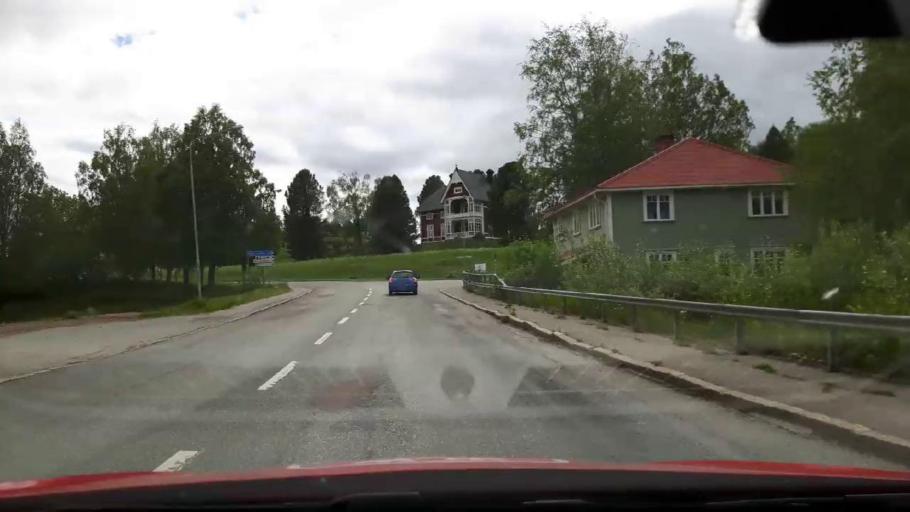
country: SE
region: Jaemtland
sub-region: Ragunda Kommun
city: Hammarstrand
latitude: 63.1125
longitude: 16.3532
